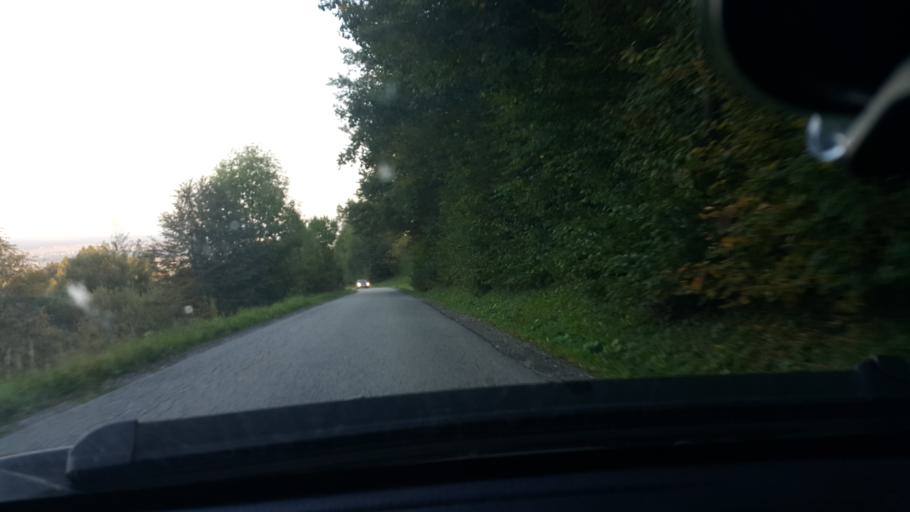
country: SI
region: Race-Fram
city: Fram
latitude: 46.4606
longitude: 15.6150
